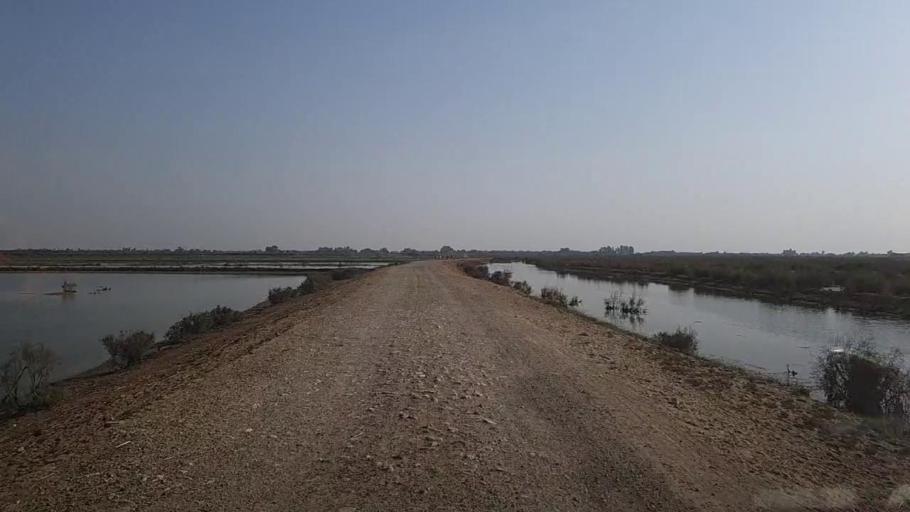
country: PK
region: Sindh
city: Kandhkot
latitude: 28.3645
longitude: 69.3297
